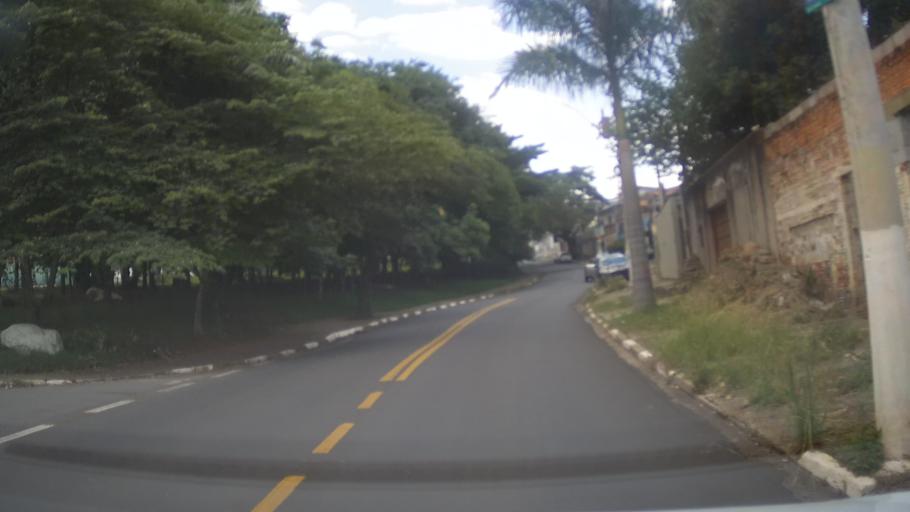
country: BR
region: Sao Paulo
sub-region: Campinas
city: Campinas
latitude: -22.9194
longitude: -47.0367
